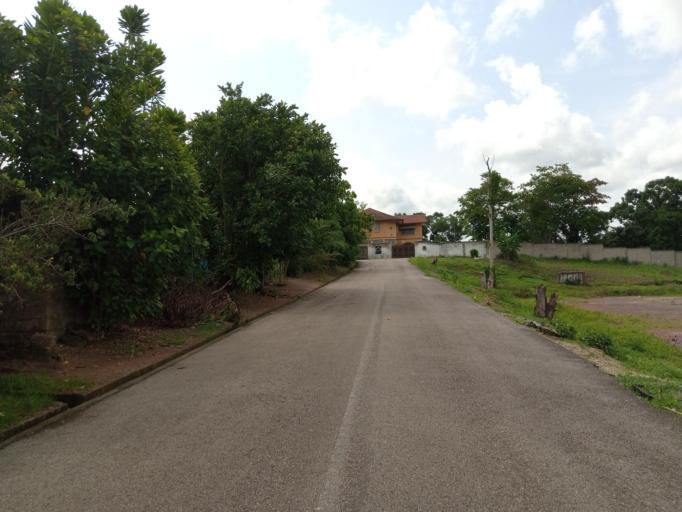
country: SL
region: Southern Province
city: Bo
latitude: 7.9829
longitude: -11.7360
